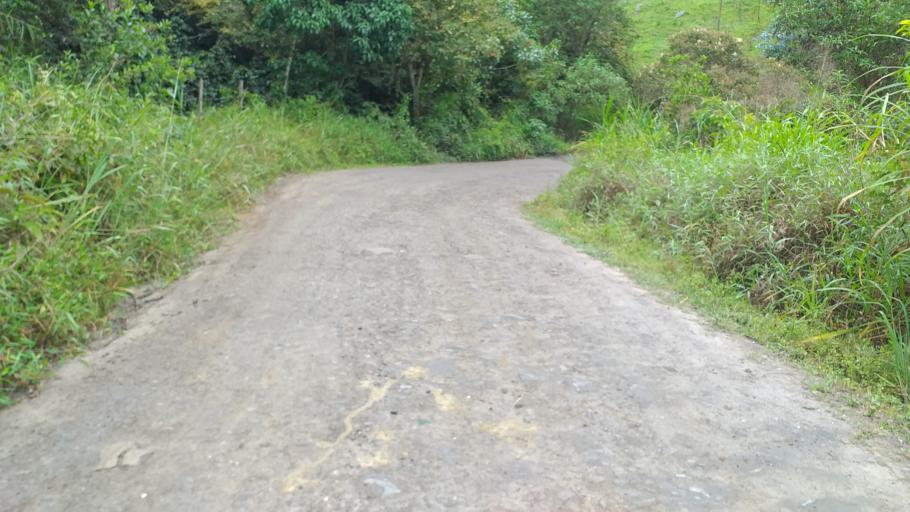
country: CO
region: Cundinamarca
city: Tenza
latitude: 5.1028
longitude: -73.4506
